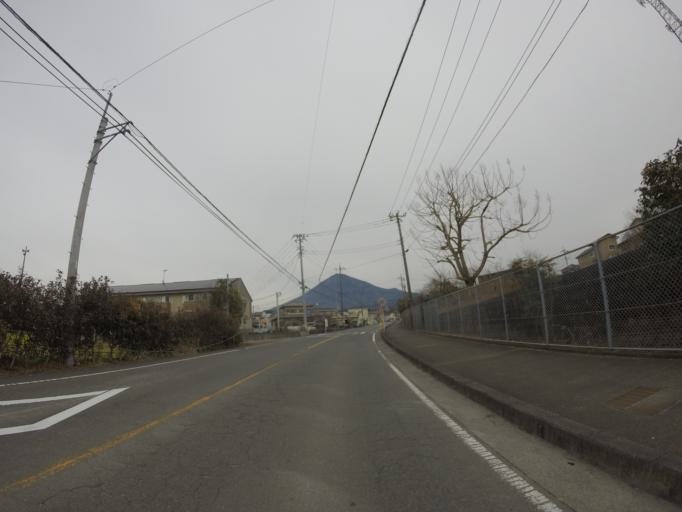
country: JP
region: Shizuoka
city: Fujinomiya
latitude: 35.2468
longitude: 138.6299
